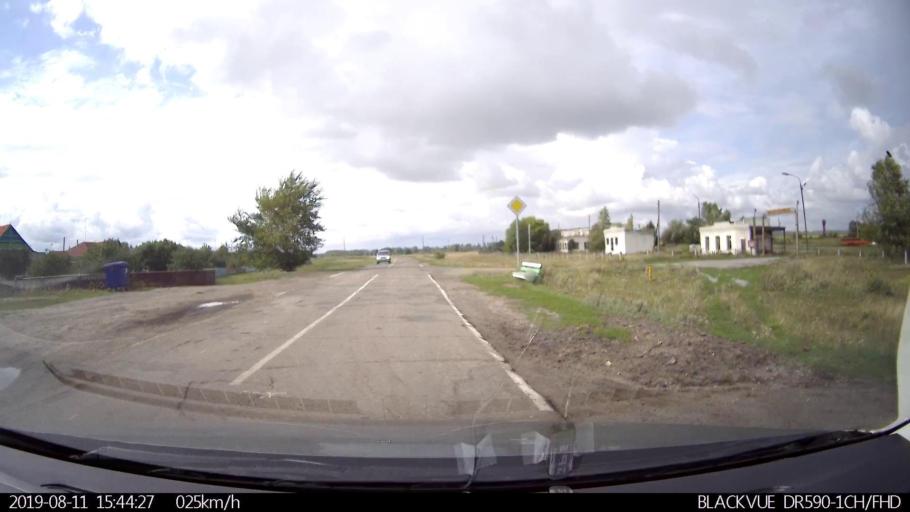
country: RU
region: Ulyanovsk
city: Ignatovka
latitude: 53.8817
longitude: 47.6567
